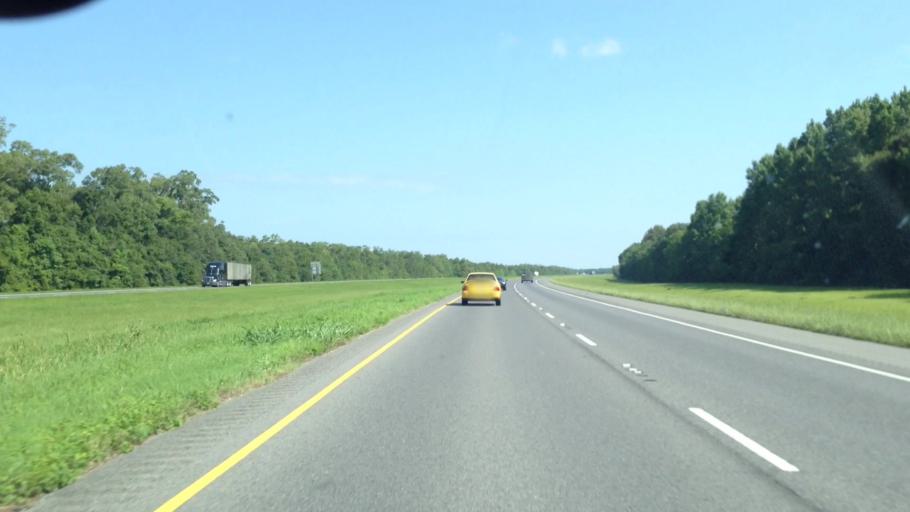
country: US
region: Louisiana
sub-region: Saint Landry Parish
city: Opelousas
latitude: 30.6668
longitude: -92.0702
